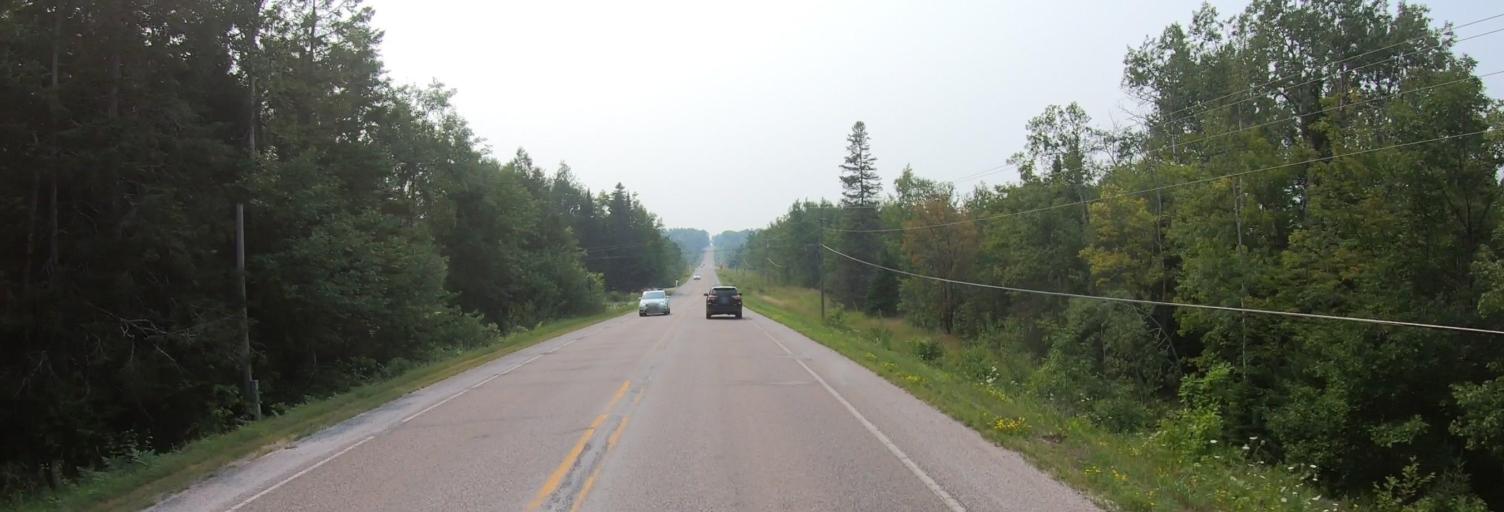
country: US
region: Michigan
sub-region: Chippewa County
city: Sault Ste. Marie
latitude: 46.4629
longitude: -84.3164
